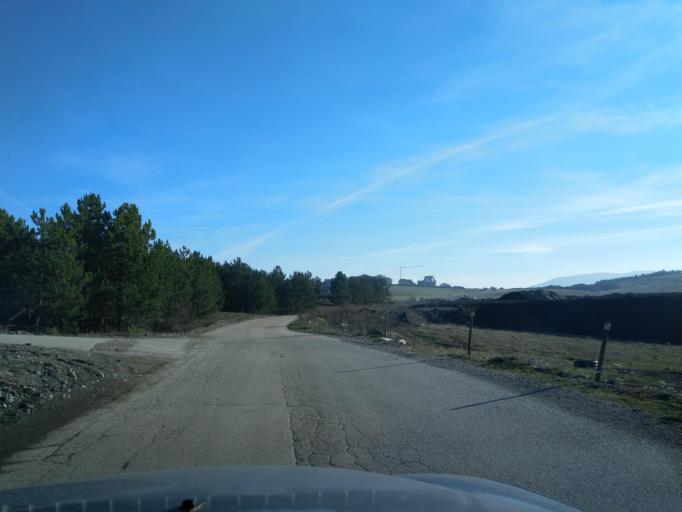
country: RS
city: Zlatibor
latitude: 43.7328
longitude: 19.6807
